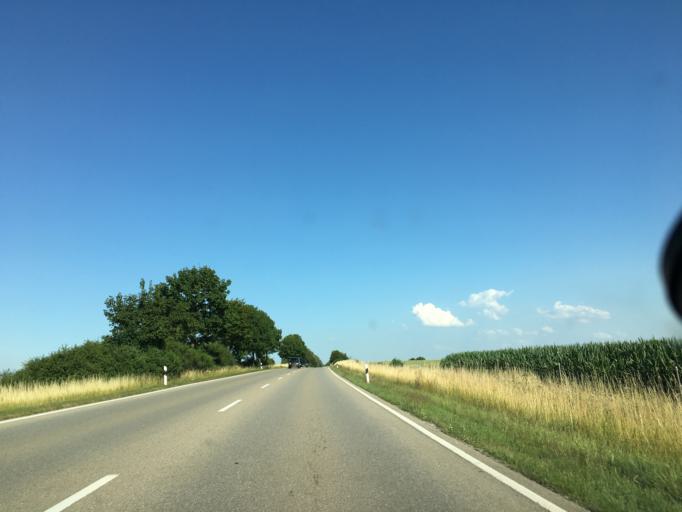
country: DE
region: Bavaria
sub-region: Upper Bavaria
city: Stammham
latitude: 48.2867
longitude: 11.8754
